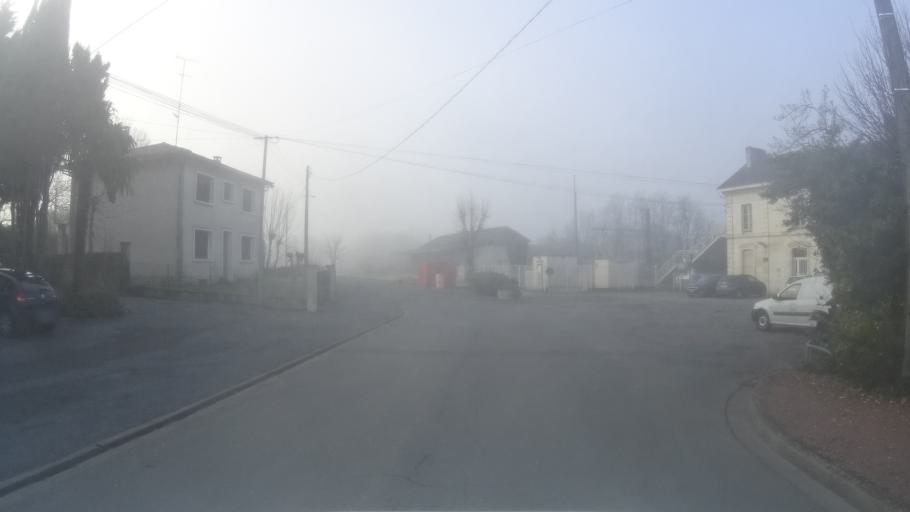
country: FR
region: Poitou-Charentes
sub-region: Departement de la Charente-Maritime
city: Saint-Aigulin
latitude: 45.1575
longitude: -0.0186
